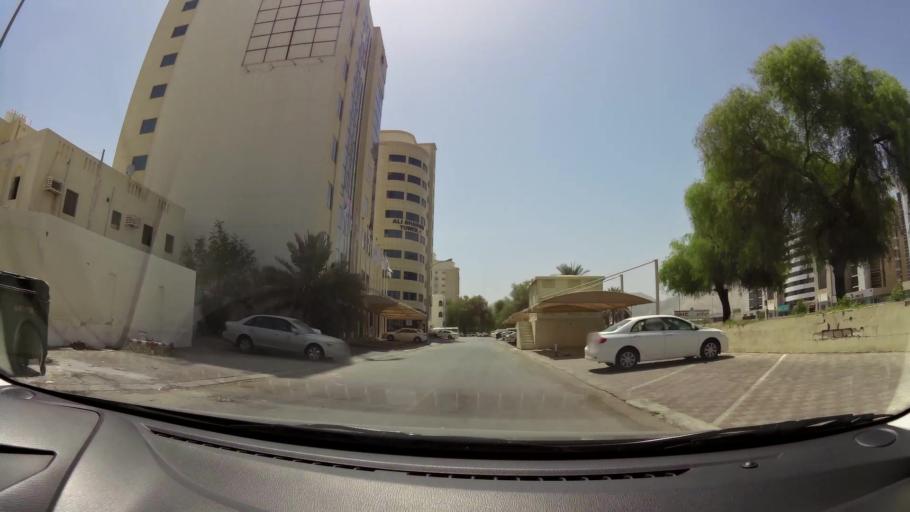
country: OM
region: Muhafazat Masqat
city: Bawshar
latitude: 23.5836
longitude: 58.3981
